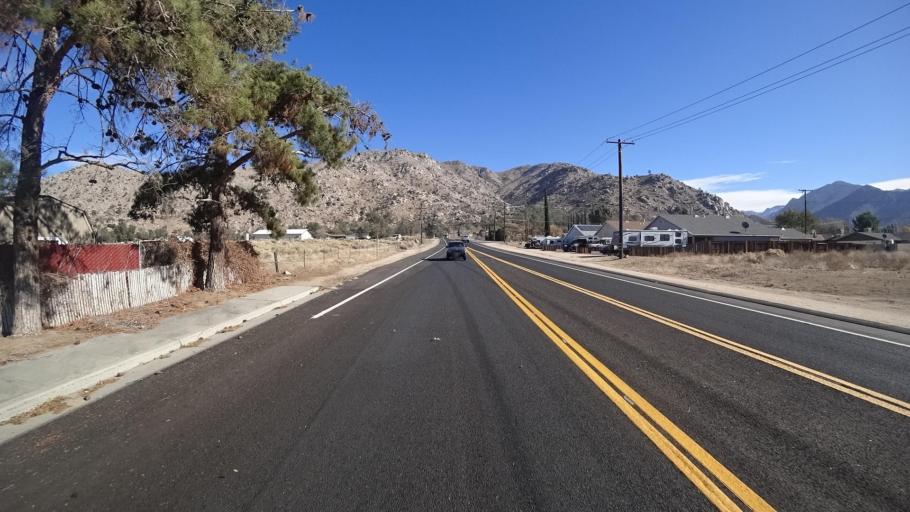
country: US
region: California
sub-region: Kern County
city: Lake Isabella
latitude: 35.6168
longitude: -118.4682
